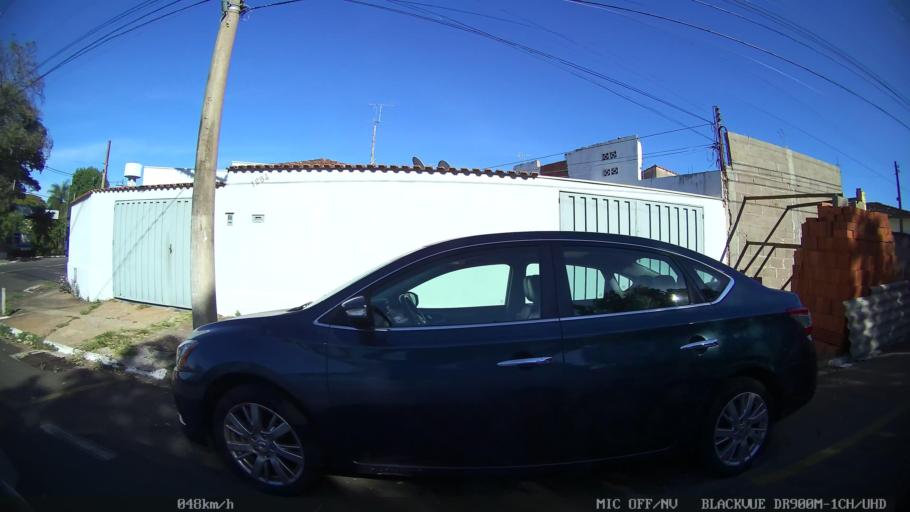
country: BR
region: Sao Paulo
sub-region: Franca
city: Franca
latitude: -20.5474
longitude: -47.4125
